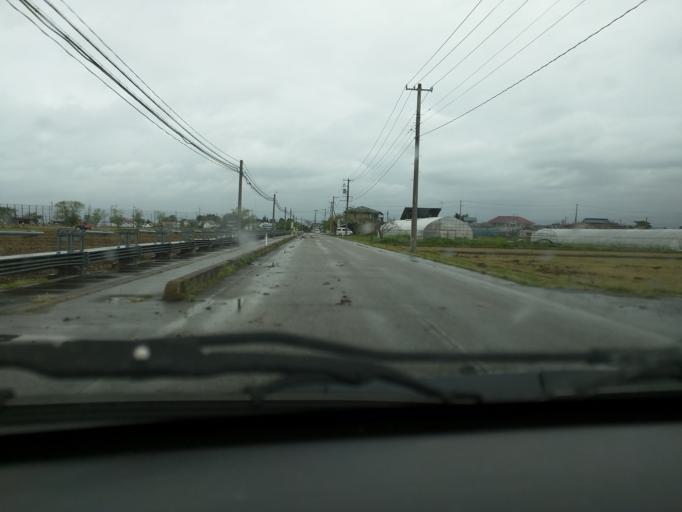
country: JP
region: Fukushima
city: Kitakata
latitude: 37.5678
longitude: 139.8734
